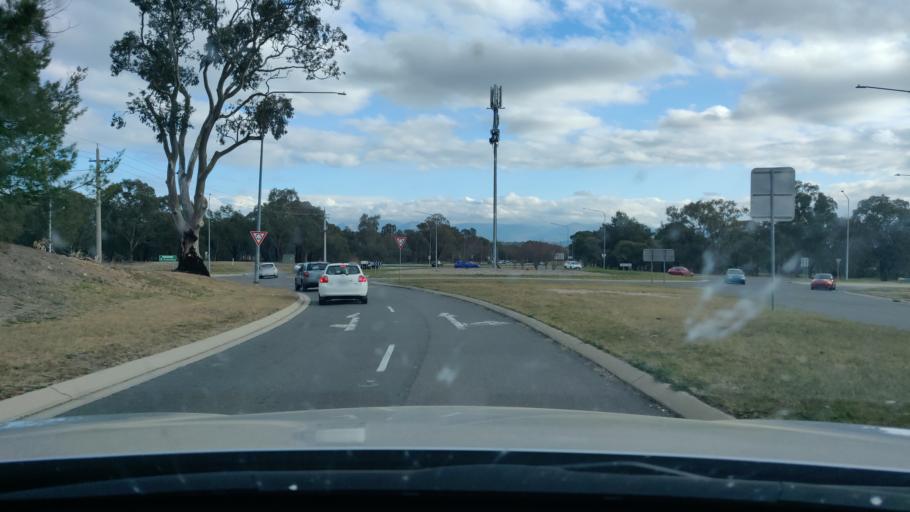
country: AU
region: Australian Capital Territory
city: Macarthur
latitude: -35.4161
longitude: 149.1154
